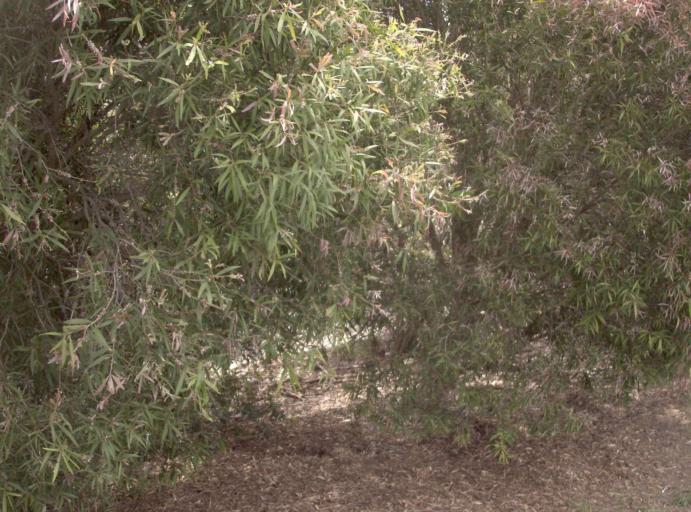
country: AU
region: Victoria
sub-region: Mornington Peninsula
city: Rosebud West
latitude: -38.3721
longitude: 144.8891
